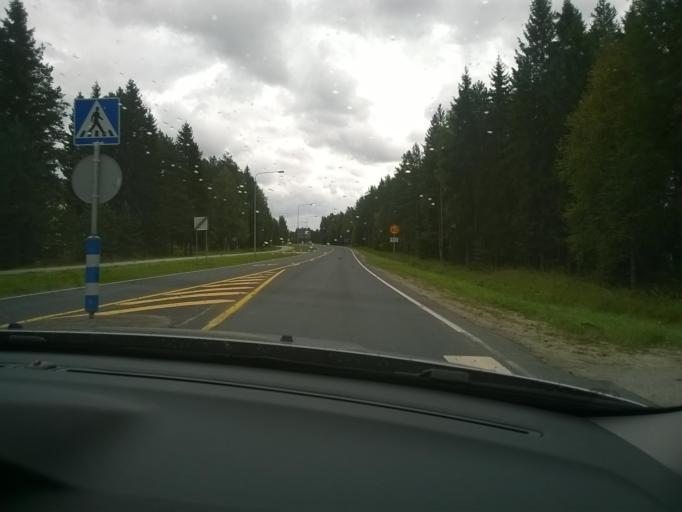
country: FI
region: Kainuu
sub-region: Kehys-Kainuu
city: Kuhmo
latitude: 64.1220
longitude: 29.5095
